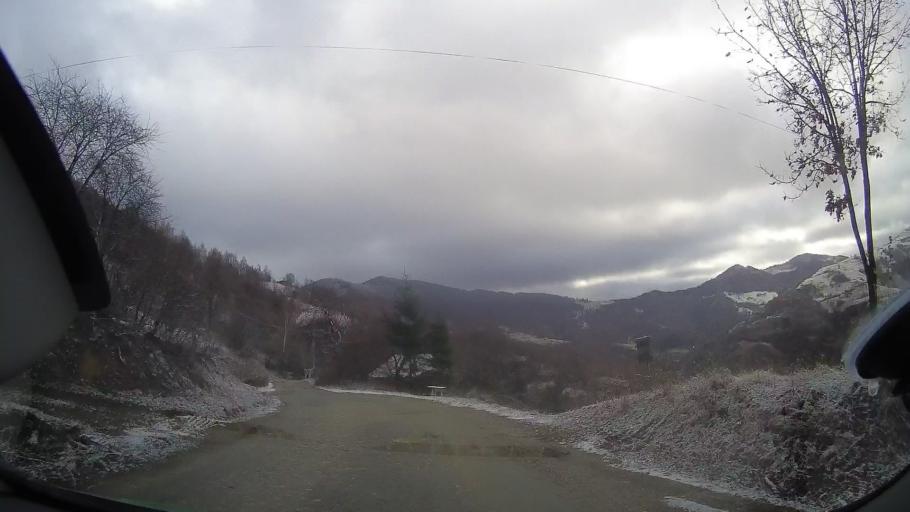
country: RO
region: Cluj
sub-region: Comuna Valea Ierii
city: Valea Ierii
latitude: 46.6766
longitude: 23.3178
